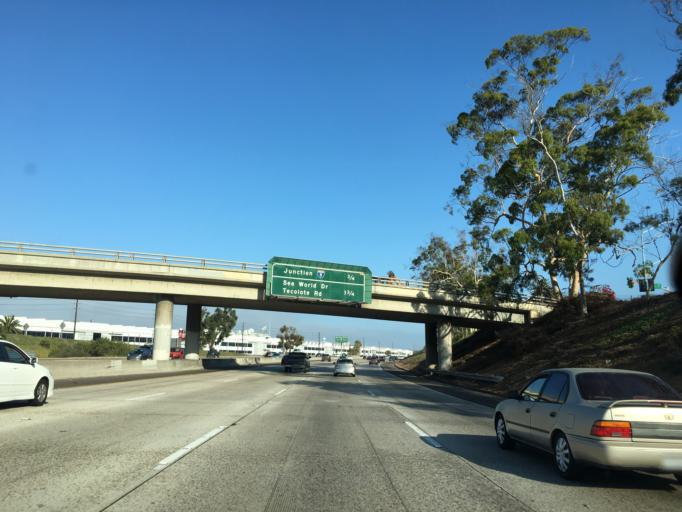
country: US
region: California
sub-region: San Diego County
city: San Diego
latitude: 32.7474
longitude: -117.1929
